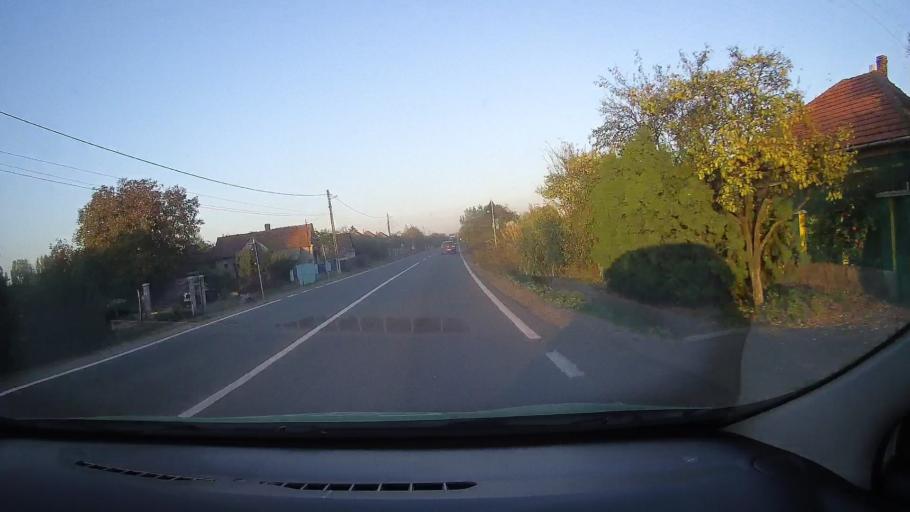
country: RO
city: Dioszeg
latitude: 47.2824
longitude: 21.9868
